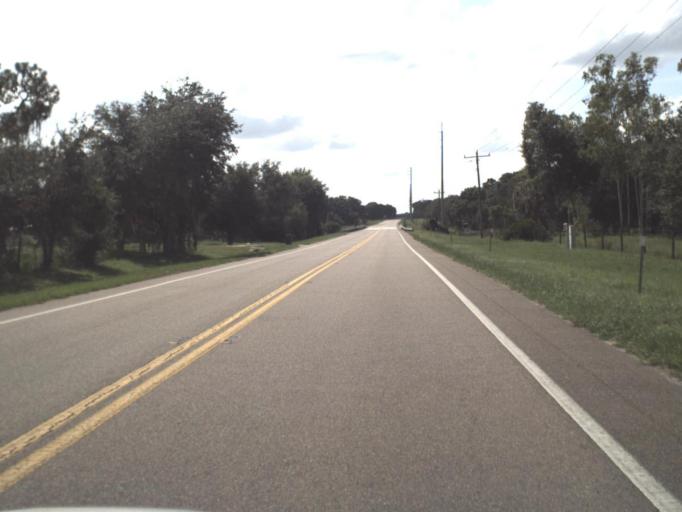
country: US
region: Florida
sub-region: Hardee County
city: Wauchula
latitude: 27.4877
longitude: -82.0210
